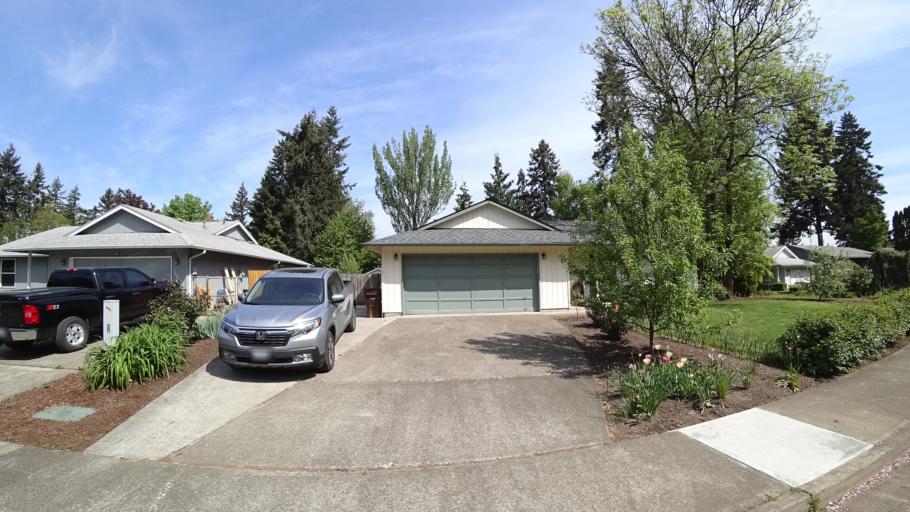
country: US
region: Oregon
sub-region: Washington County
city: Hillsboro
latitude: 45.5152
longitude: -122.9401
